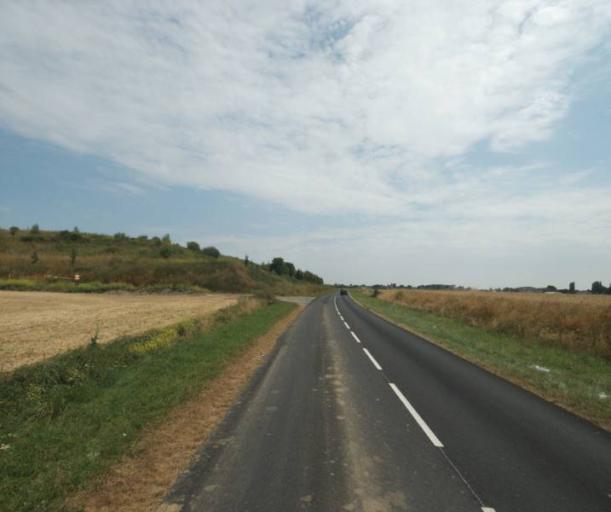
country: FR
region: Nord-Pas-de-Calais
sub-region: Departement du Nord
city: Marquillies
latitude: 50.5613
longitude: 2.8784
